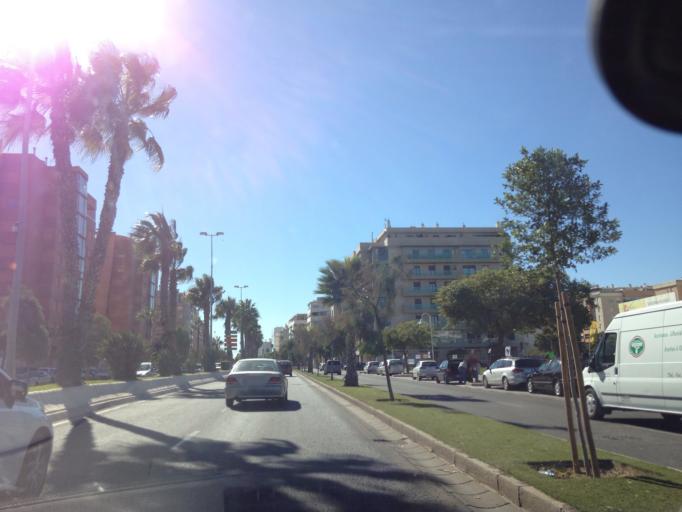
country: ES
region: Andalusia
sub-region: Provincia de Malaga
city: Malaga
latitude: 36.6958
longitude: -4.4394
